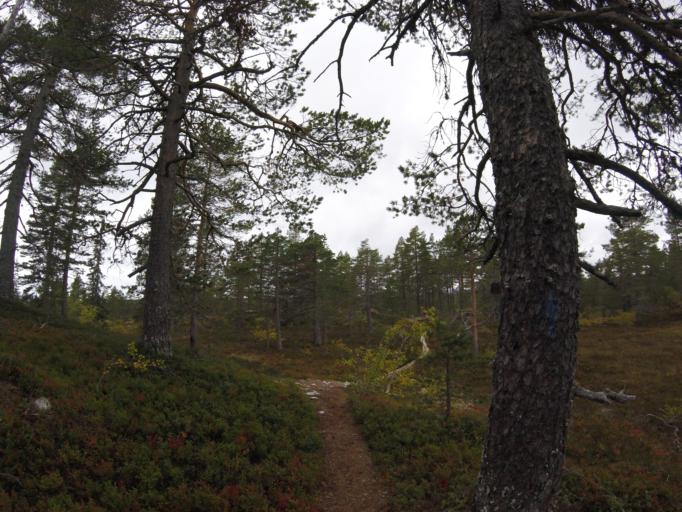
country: NO
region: Buskerud
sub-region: Flesberg
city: Lampeland
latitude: 59.7581
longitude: 9.3940
